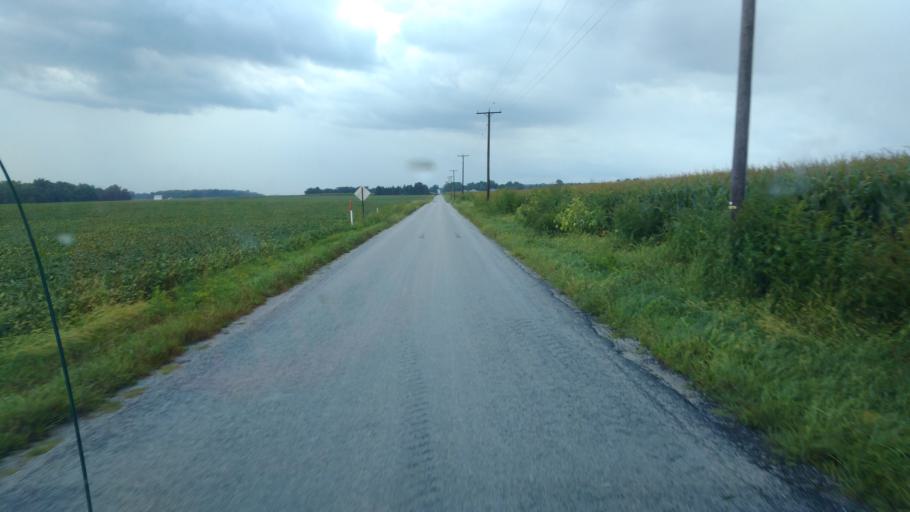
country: US
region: Ohio
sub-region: Hardin County
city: Kenton
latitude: 40.6741
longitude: -83.5943
